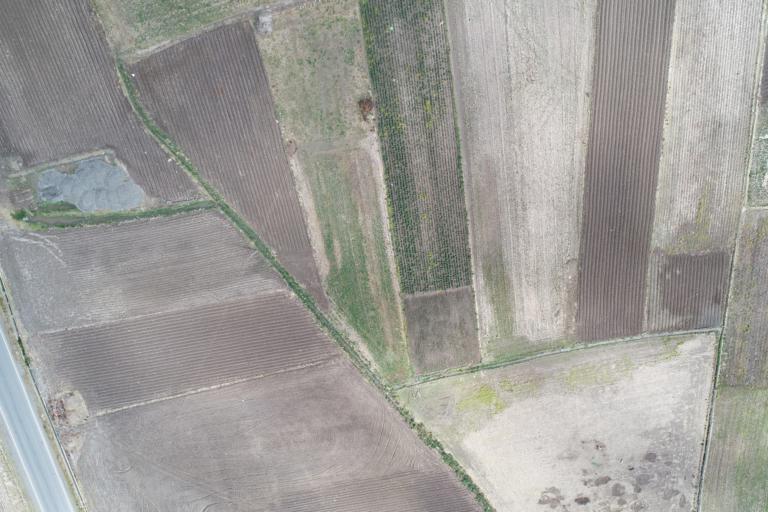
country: BO
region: La Paz
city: Achacachi
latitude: -16.0296
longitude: -68.6879
